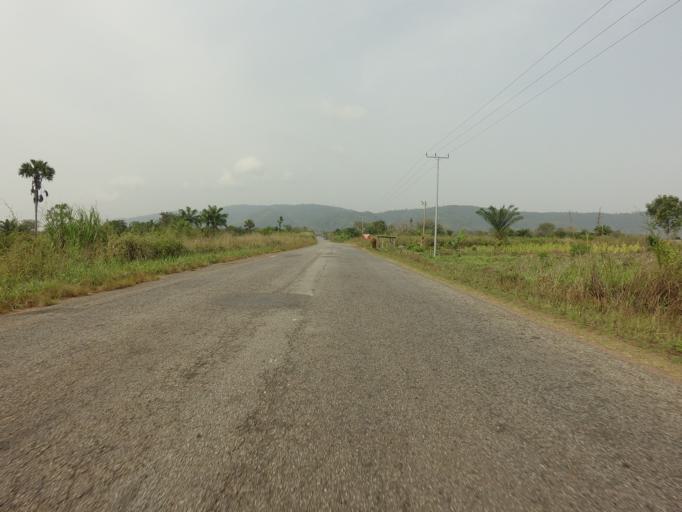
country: GH
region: Volta
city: Ho
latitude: 6.5755
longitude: 0.3281
